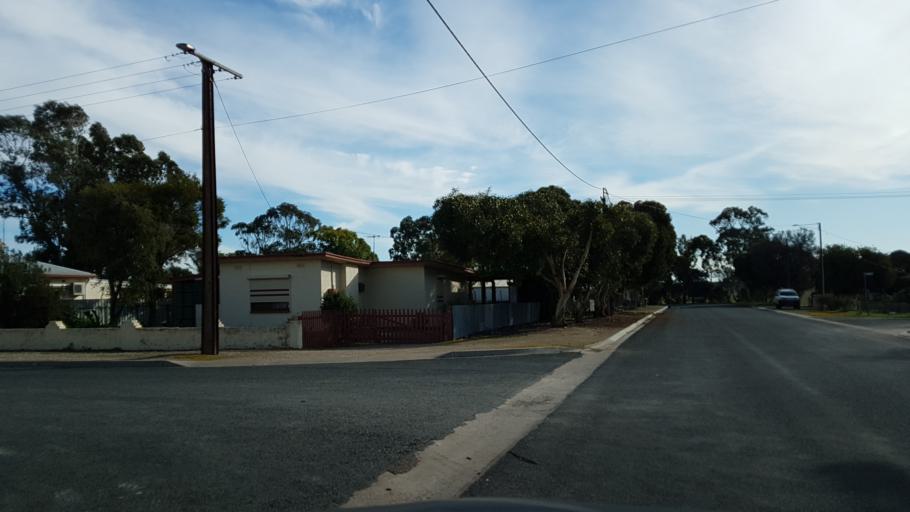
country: AU
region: South Australia
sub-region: Murray Bridge
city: Tailem Bend
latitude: -35.2518
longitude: 139.4625
